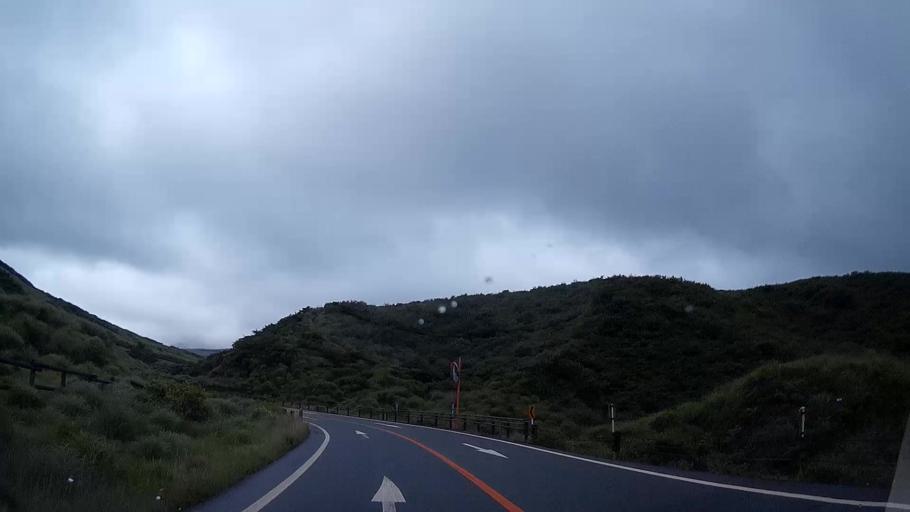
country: JP
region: Kumamoto
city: Aso
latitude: 32.8850
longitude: 131.0597
